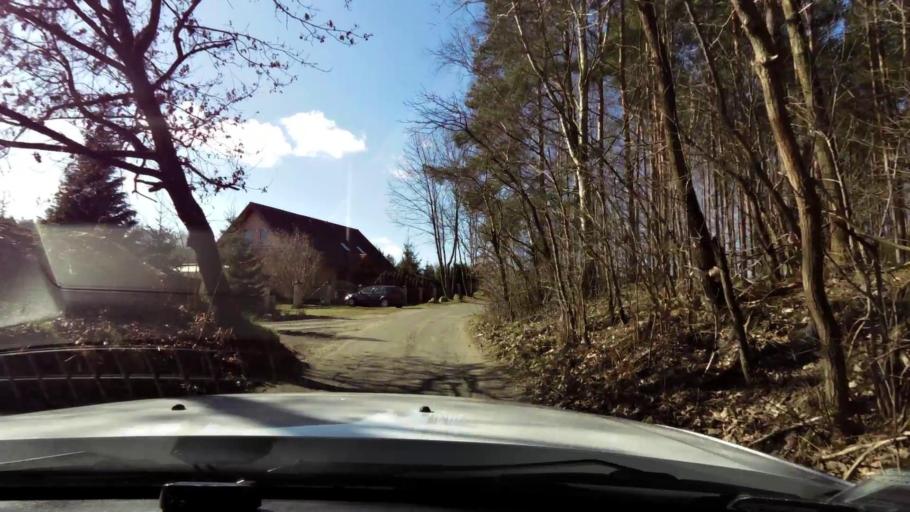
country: PL
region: West Pomeranian Voivodeship
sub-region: Powiat gryfinski
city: Gryfino
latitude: 53.2179
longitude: 14.5154
